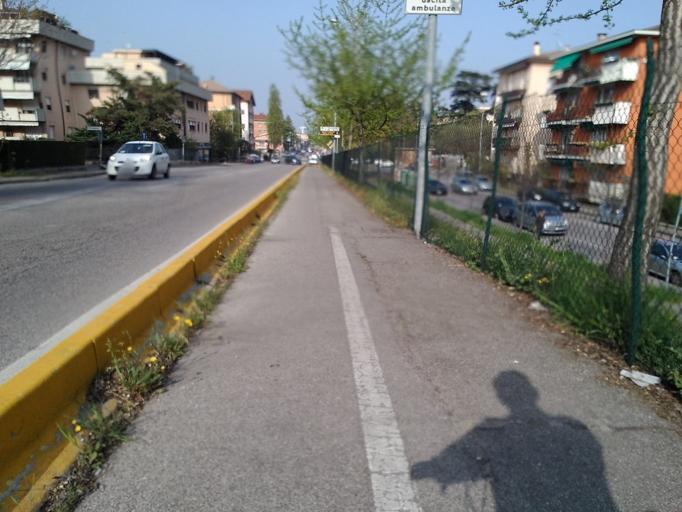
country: IT
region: Veneto
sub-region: Provincia di Verona
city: Verona
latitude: 45.4189
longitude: 10.9503
